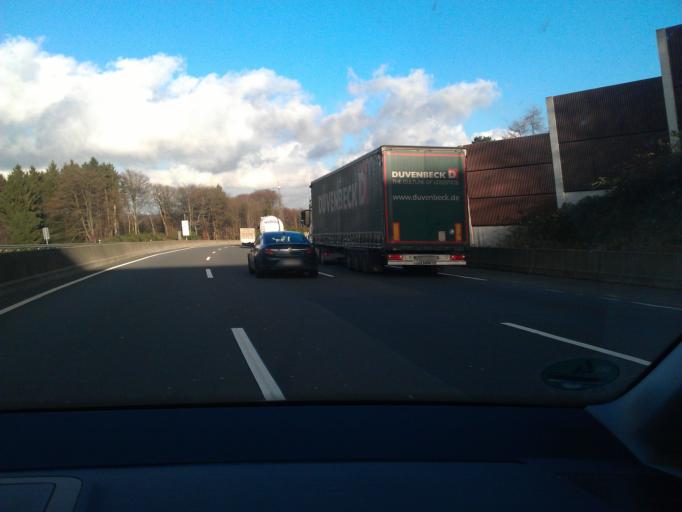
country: DE
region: North Rhine-Westphalia
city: Wermelskirchen
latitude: 51.1383
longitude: 7.1910
